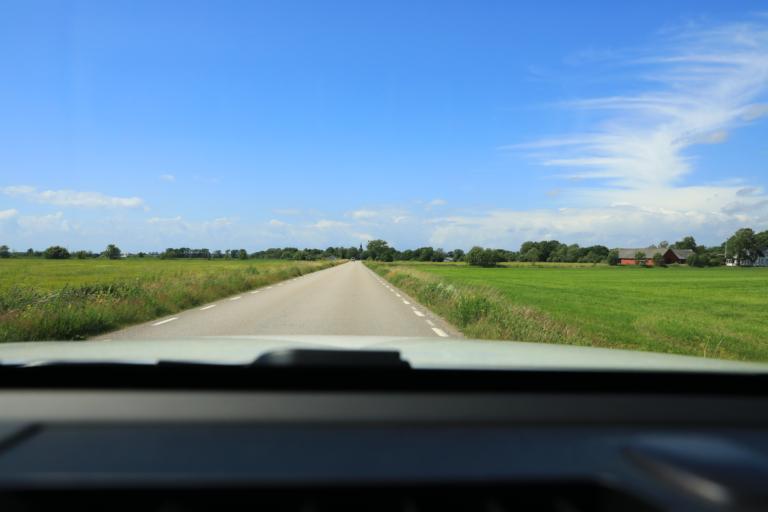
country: SE
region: Halland
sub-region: Varbergs Kommun
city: Tvaaker
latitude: 57.0982
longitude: 12.3773
